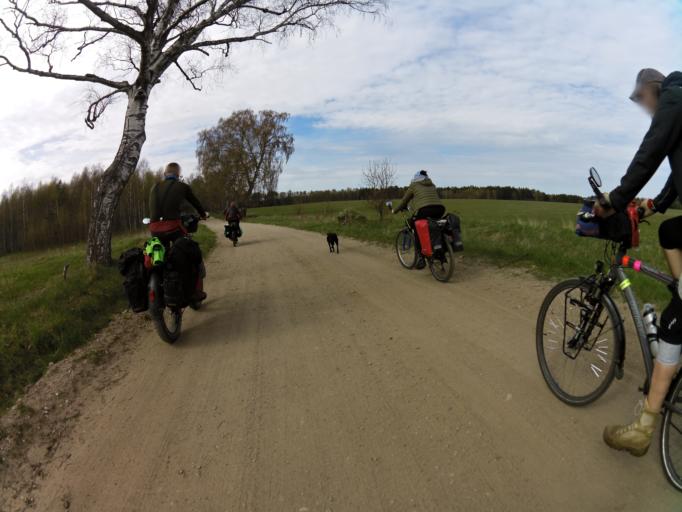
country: PL
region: West Pomeranian Voivodeship
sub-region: Powiat koszalinski
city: Bobolice
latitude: 53.8535
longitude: 16.6866
